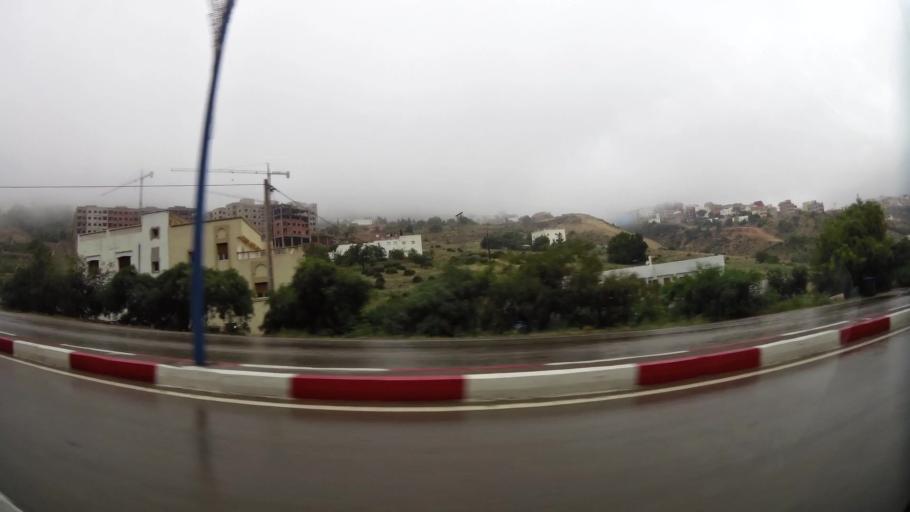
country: MA
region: Taza-Al Hoceima-Taounate
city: Al Hoceima
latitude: 35.2278
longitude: -3.9303
